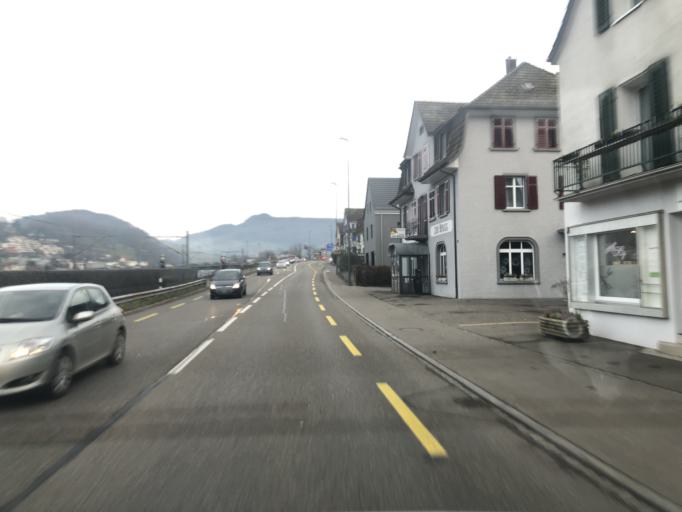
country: CH
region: Aargau
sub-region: Bezirk Baden
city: Obersiggenthal
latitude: 47.4832
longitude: 8.2949
